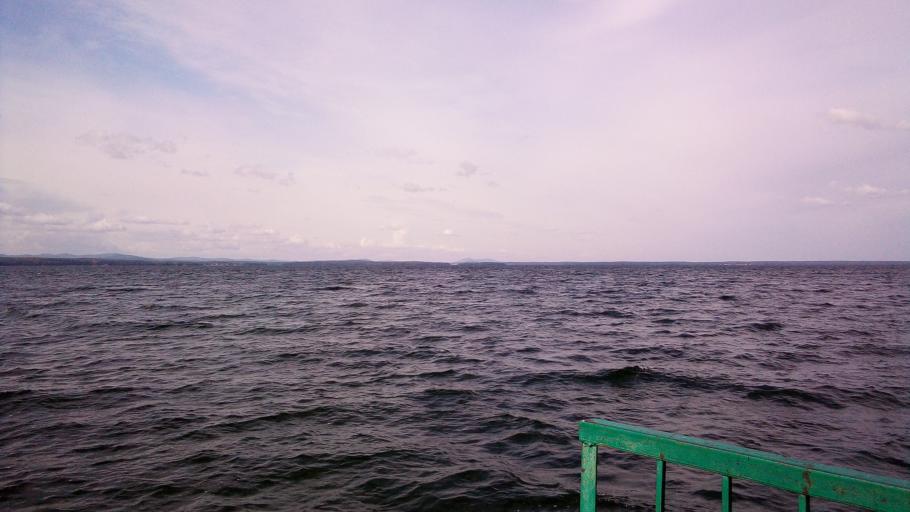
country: RU
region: Chelyabinsk
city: Tayginka
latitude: 55.4768
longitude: 60.4891
